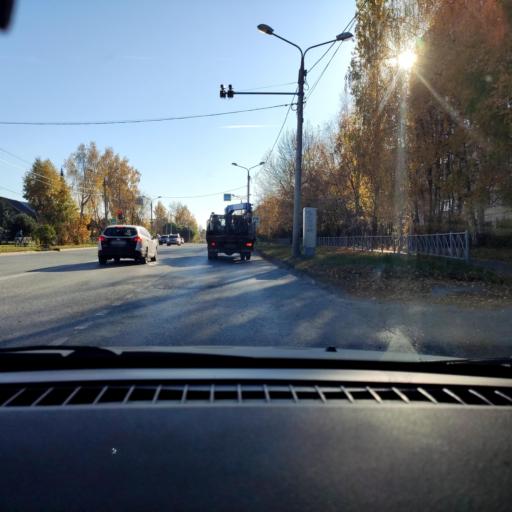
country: RU
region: Perm
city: Perm
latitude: 58.0644
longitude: 56.3638
